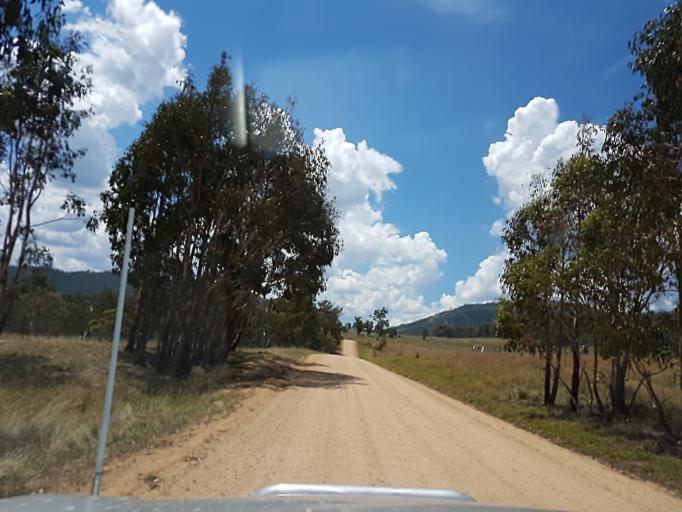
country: AU
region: Victoria
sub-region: Alpine
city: Mount Beauty
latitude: -36.8992
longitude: 147.8715
